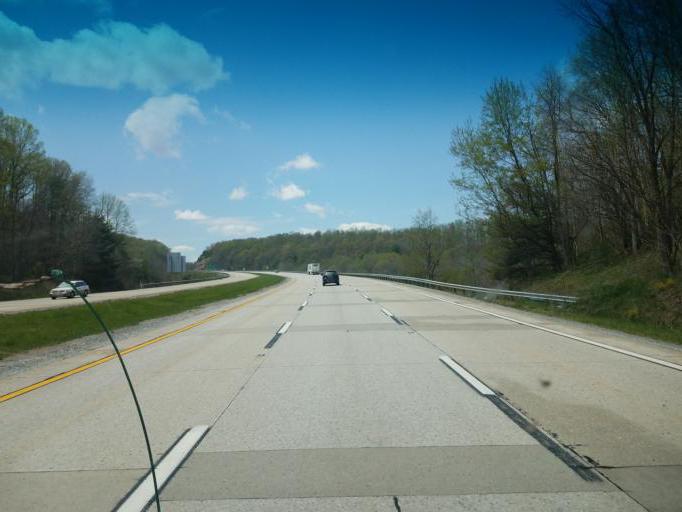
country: US
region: West Virginia
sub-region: Raleigh County
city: Beaver
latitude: 37.7487
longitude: -81.1599
